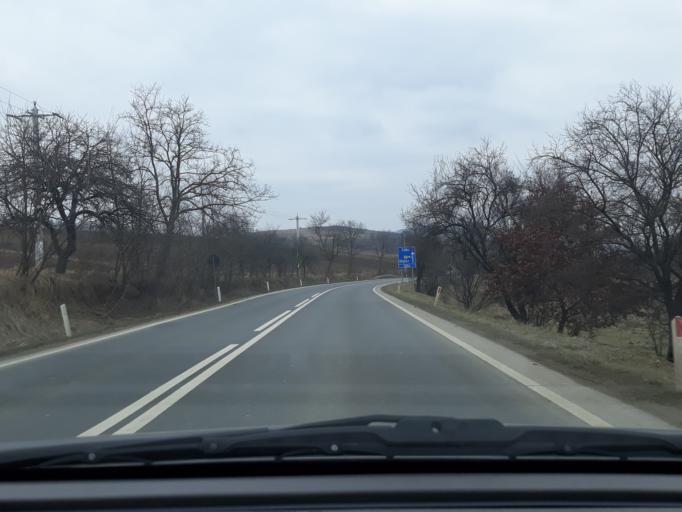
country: RO
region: Salaj
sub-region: Comuna Nusfalau
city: Nusfalau
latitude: 47.2180
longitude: 22.7262
